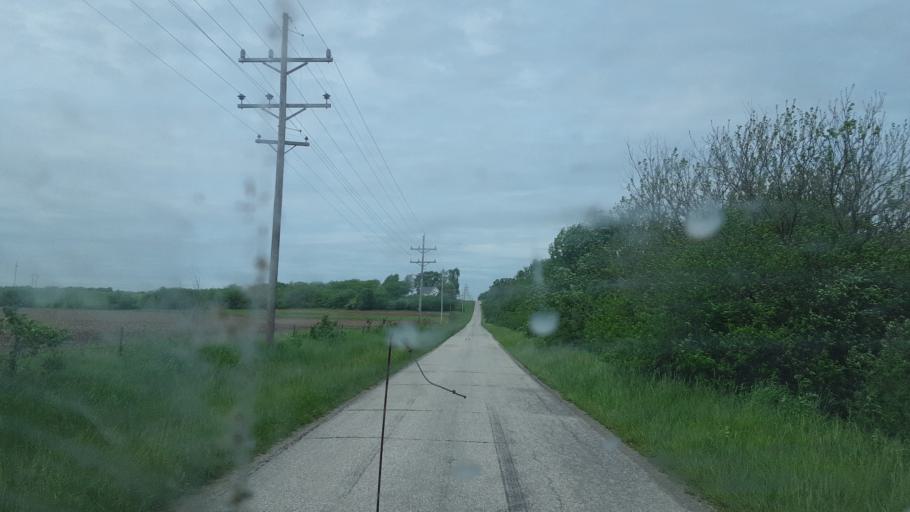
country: US
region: Missouri
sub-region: Clark County
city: Kahoka
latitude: 40.4238
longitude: -91.5814
